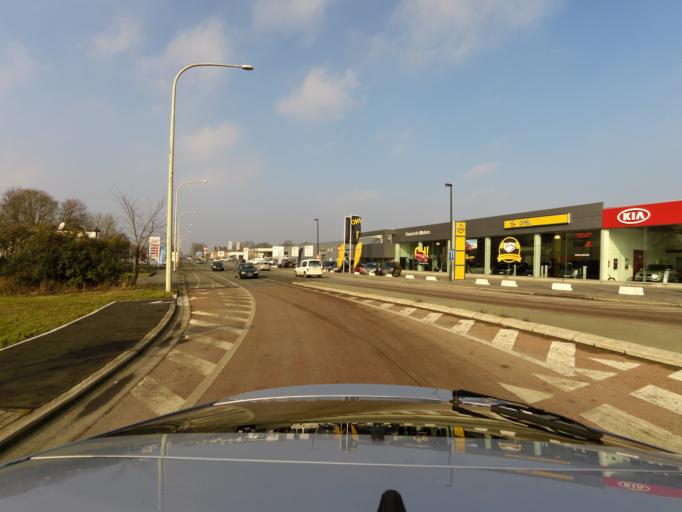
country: BE
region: Wallonia
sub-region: Province du Hainaut
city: Tournai
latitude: 50.6022
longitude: 3.4286
